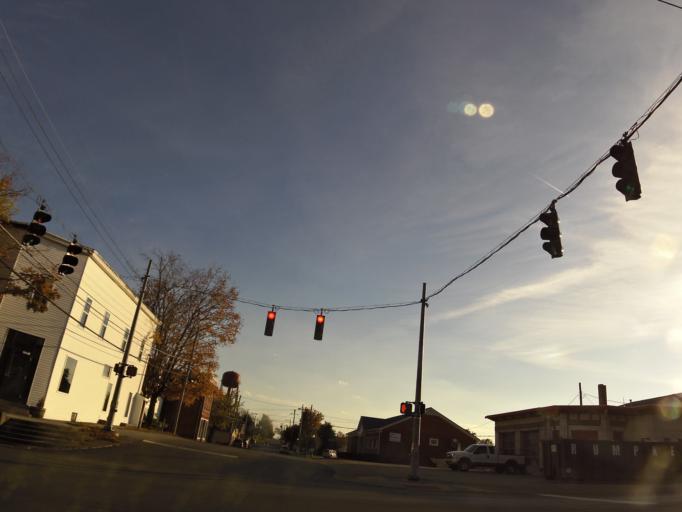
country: US
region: Kentucky
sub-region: Garrard County
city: Lancaster
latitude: 37.6193
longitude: -84.5771
